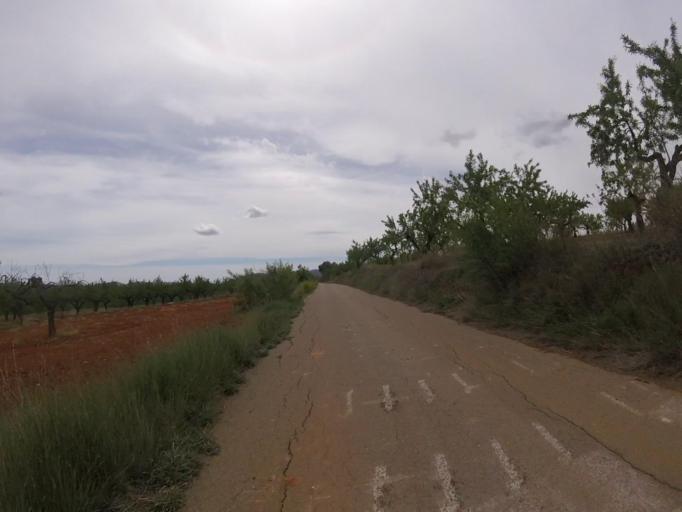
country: ES
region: Valencia
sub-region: Provincia de Castello
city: Benlloch
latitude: 40.1833
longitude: -0.0084
